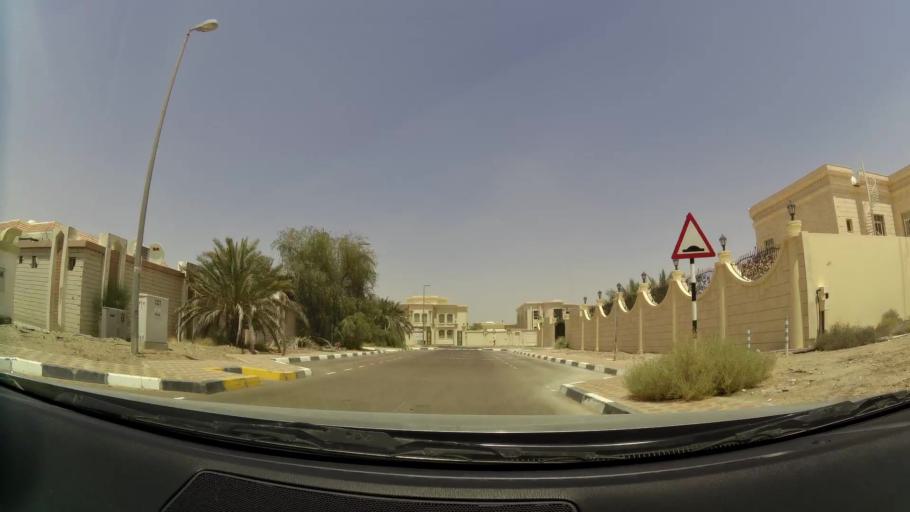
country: AE
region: Abu Dhabi
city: Al Ain
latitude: 24.2514
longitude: 55.7114
